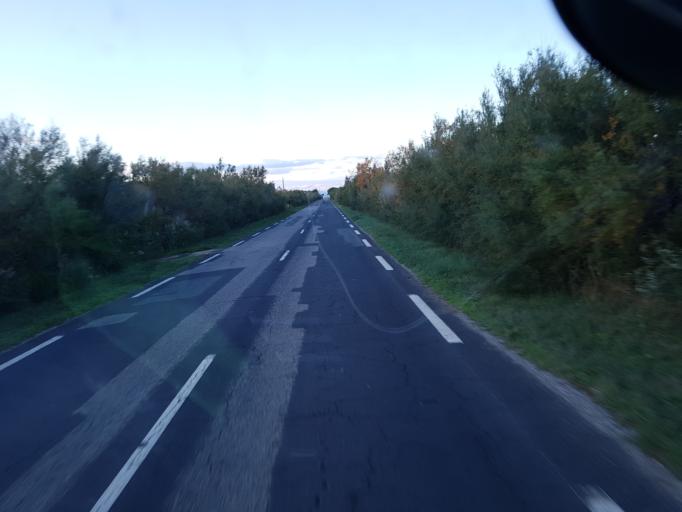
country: FR
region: Languedoc-Roussillon
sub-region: Departement de l'Aude
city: Port-la-Nouvelle
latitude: 43.0008
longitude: 3.0408
